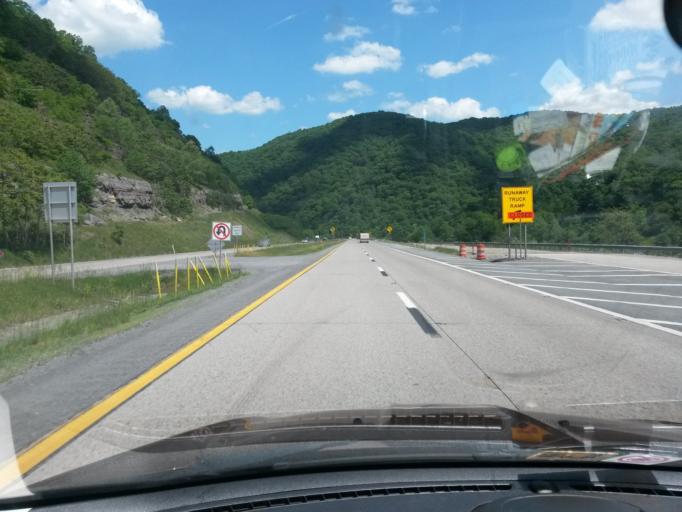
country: US
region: West Virginia
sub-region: Summers County
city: Hinton
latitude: 37.7800
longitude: -80.9351
